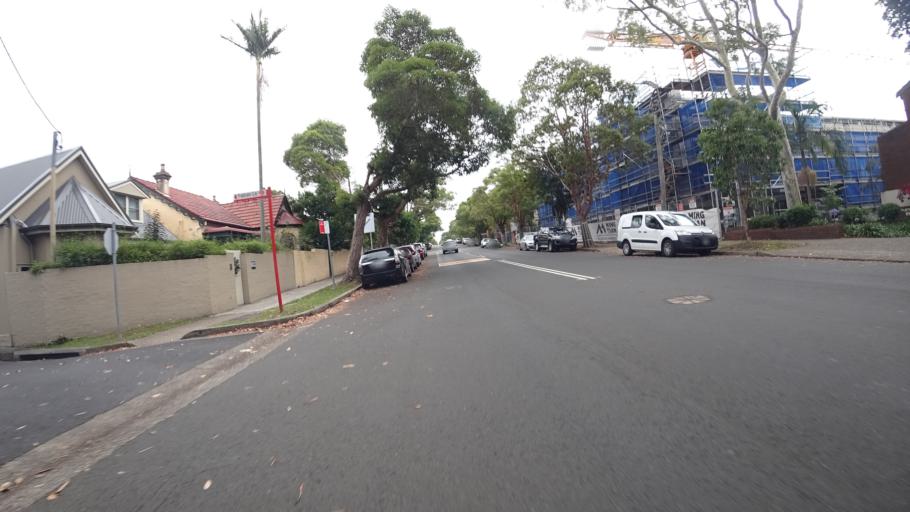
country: AU
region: New South Wales
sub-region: North Sydney
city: Crows Nest
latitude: -33.8281
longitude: 151.2064
